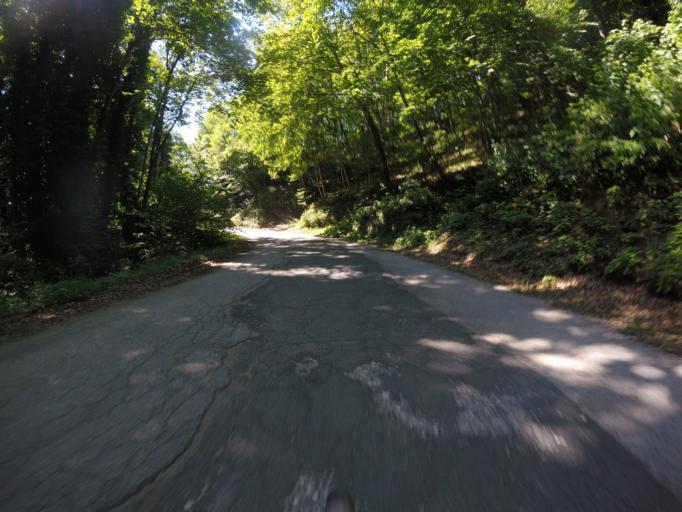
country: SI
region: Brezice
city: Brezice
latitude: 45.8359
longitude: 15.5658
